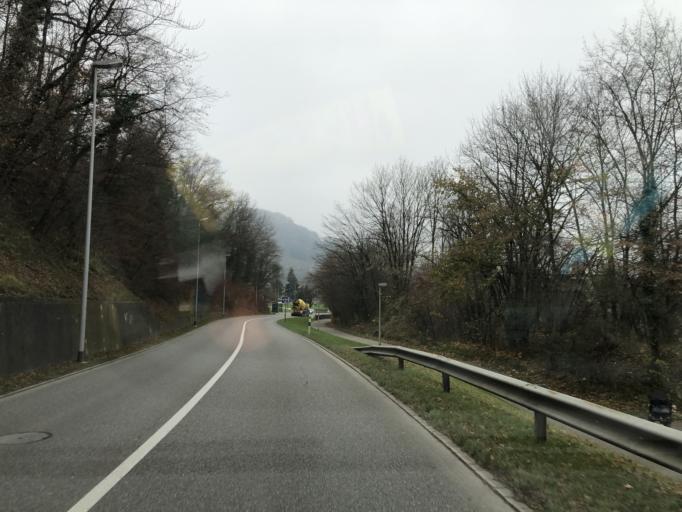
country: CH
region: Aargau
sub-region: Bezirk Baden
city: Turgi
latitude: 47.4947
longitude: 8.2658
